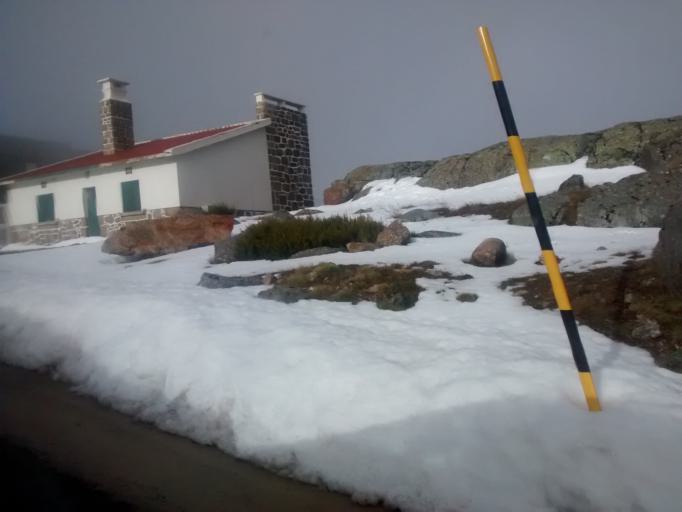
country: PT
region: Guarda
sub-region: Seia
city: Seia
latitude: 40.3657
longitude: -7.6473
